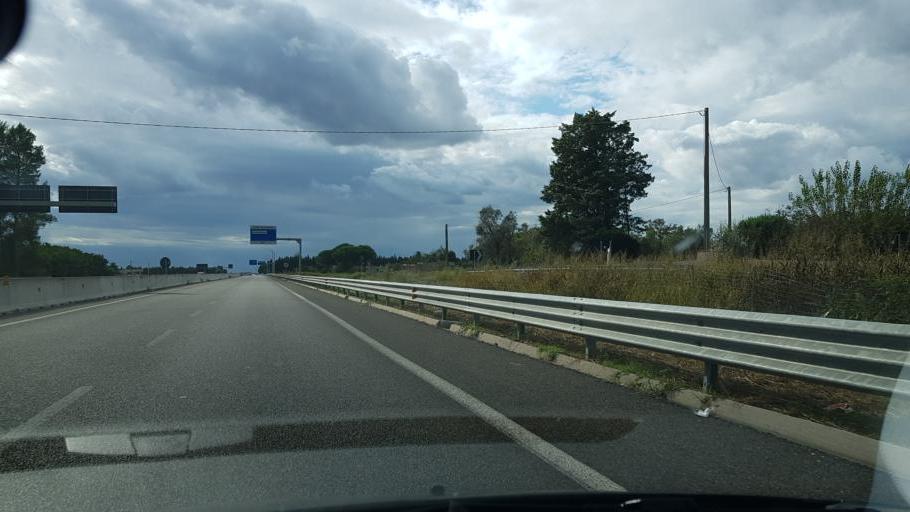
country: IT
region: Apulia
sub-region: Provincia di Lecce
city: Palmariggi
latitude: 40.1280
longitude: 18.3631
